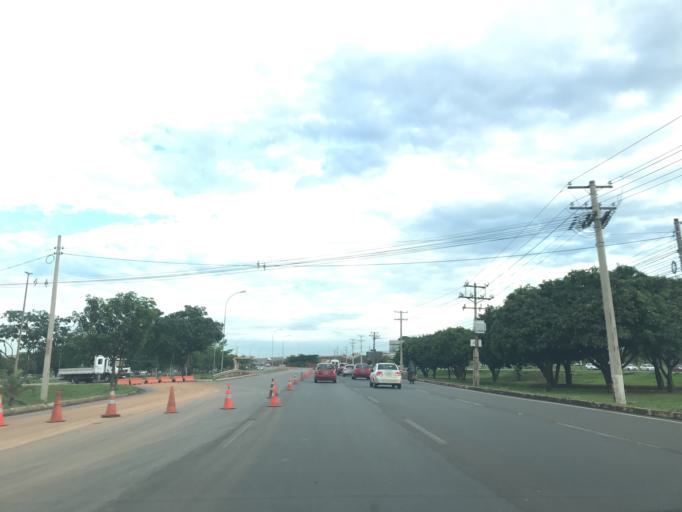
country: BR
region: Federal District
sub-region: Brasilia
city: Brasilia
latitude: -15.7787
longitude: -47.9398
